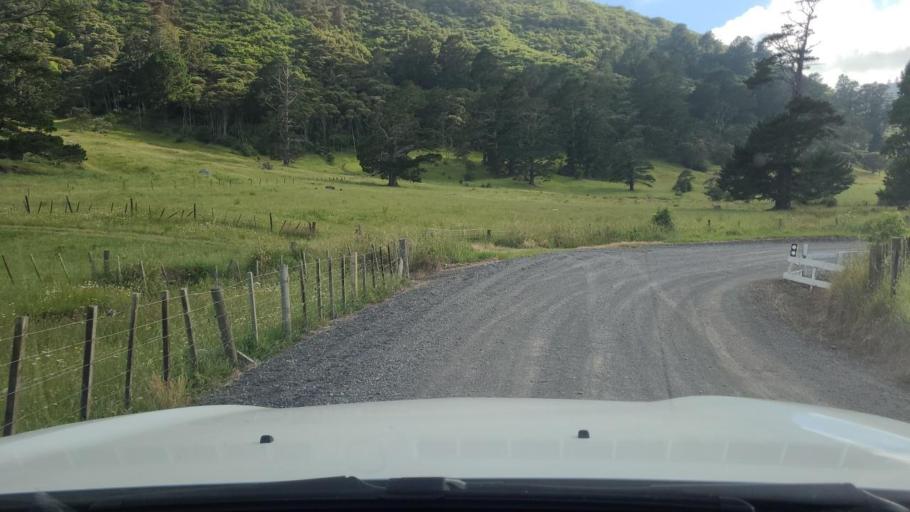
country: NZ
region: Bay of Plenty
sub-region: Western Bay of Plenty District
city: Katikati
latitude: -37.5614
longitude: 175.7453
